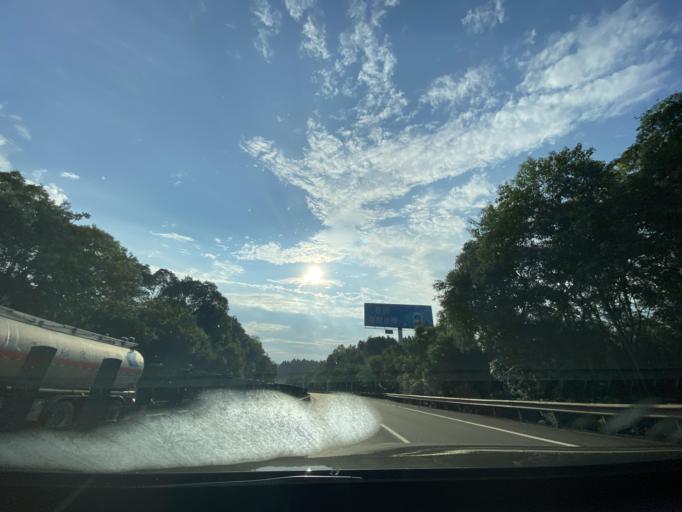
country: CN
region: Sichuan
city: Jiancheng
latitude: 30.3542
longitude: 104.5462
